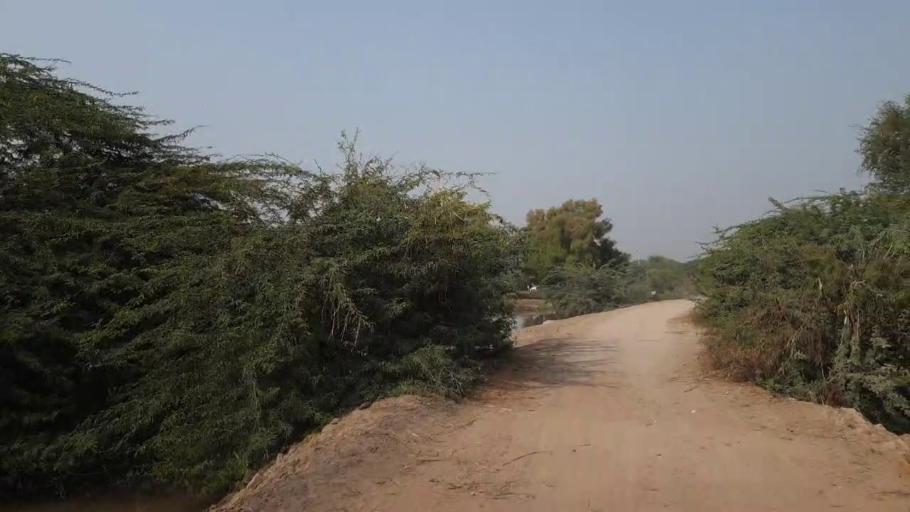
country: PK
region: Sindh
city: Bhan
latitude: 26.5401
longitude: 67.7013
